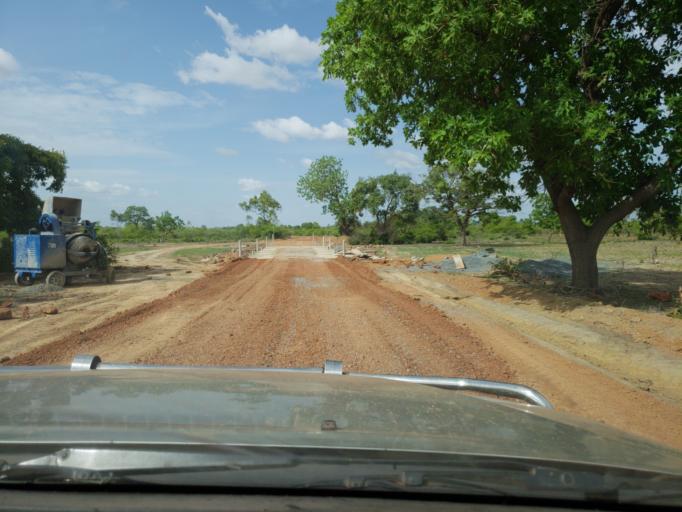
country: ML
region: Segou
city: Bla
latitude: 12.7726
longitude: -5.6156
